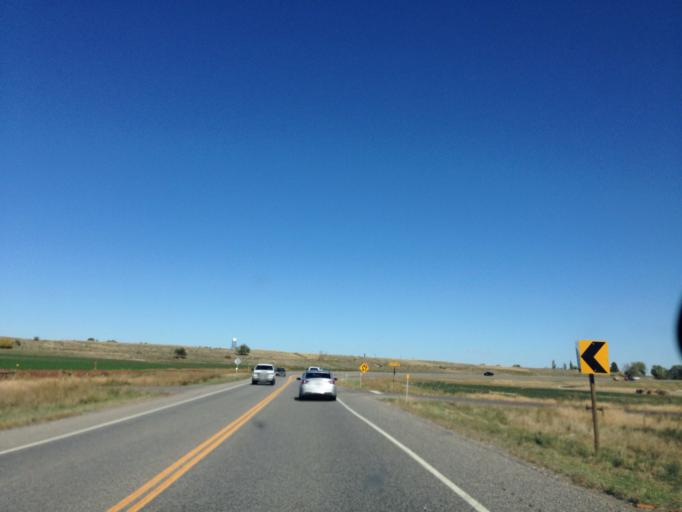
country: US
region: Montana
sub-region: Yellowstone County
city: Laurel
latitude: 45.6373
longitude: -108.7663
